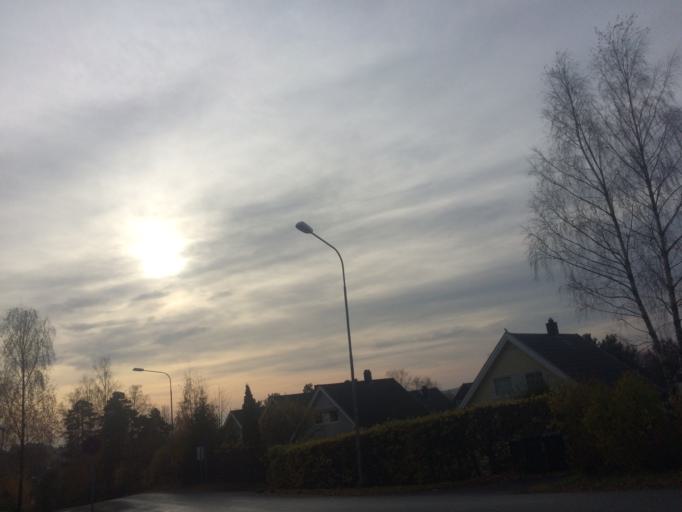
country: NO
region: Akershus
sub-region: Ski
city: Ski
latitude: 59.7270
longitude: 10.8431
